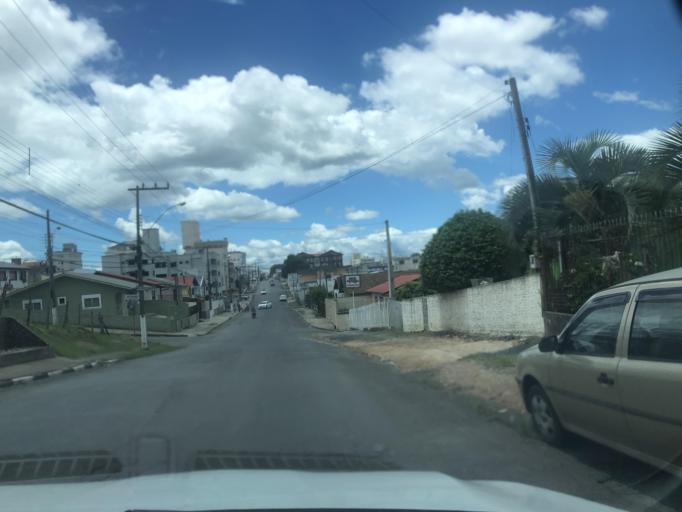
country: BR
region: Santa Catarina
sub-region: Lages
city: Lages
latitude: -27.8050
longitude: -50.3019
